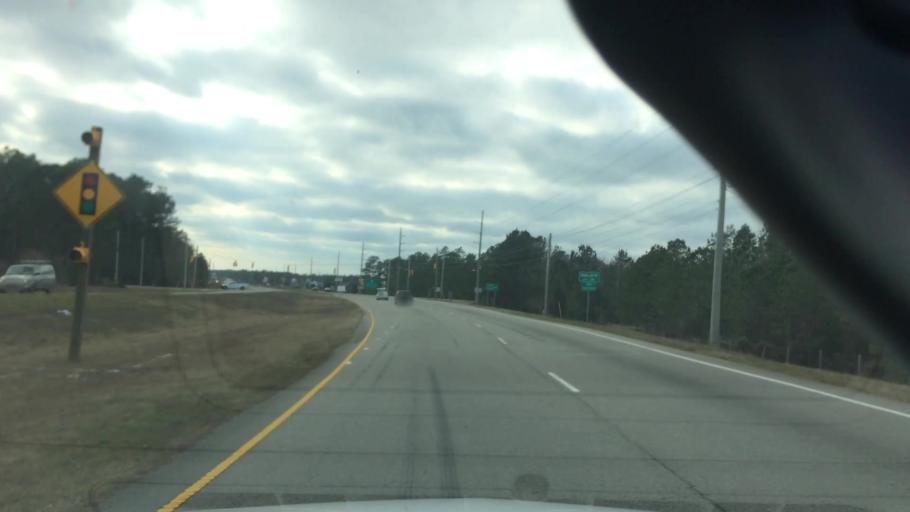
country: US
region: North Carolina
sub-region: Brunswick County
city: Shallotte
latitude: 33.9886
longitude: -78.3885
